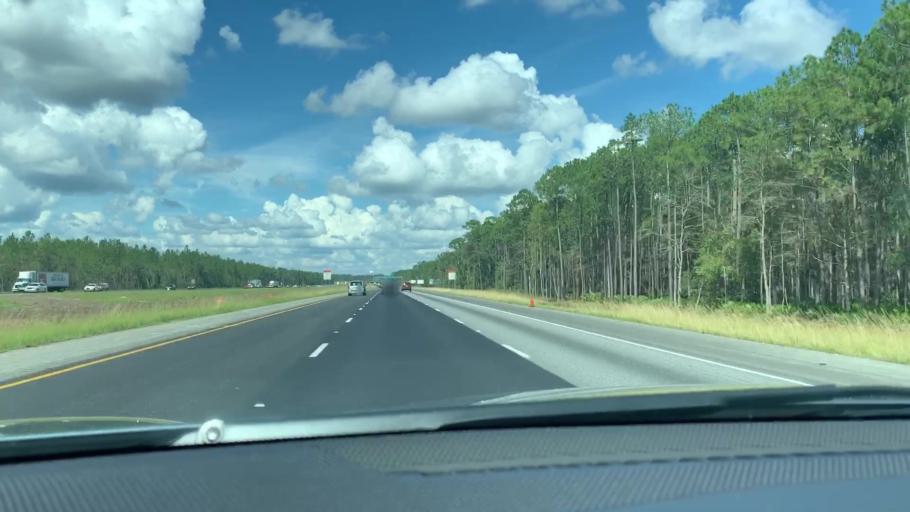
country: US
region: Georgia
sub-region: Camden County
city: Woodbine
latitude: 30.9277
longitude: -81.6858
